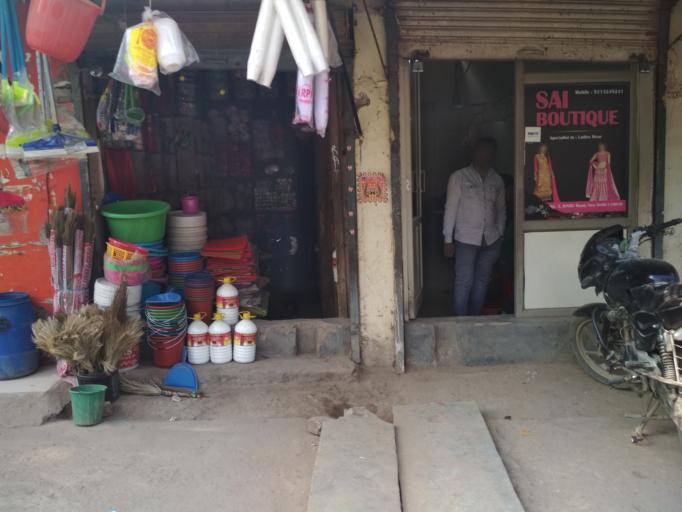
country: IN
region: NCT
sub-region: New Delhi
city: New Delhi
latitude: 28.5079
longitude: 77.2002
